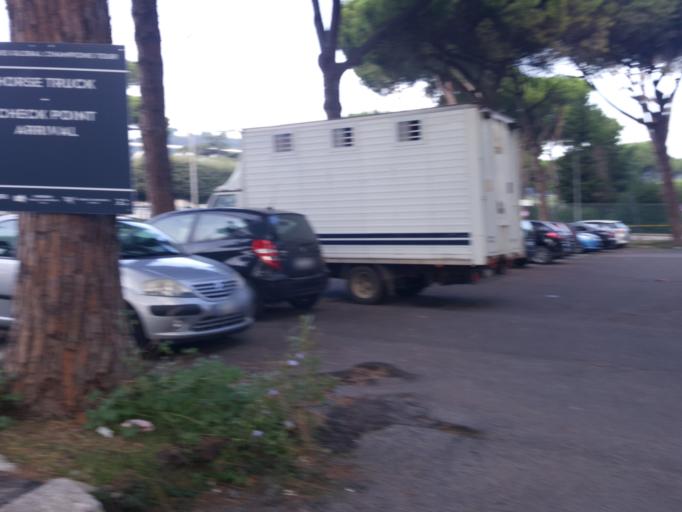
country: VA
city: Vatican City
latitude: 41.9335
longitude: 12.4606
